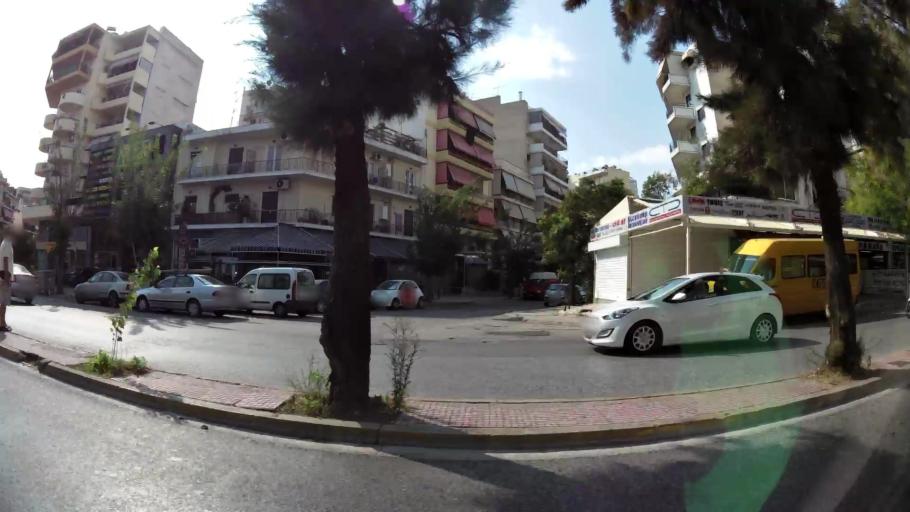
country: GR
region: Attica
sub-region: Nomarchia Athinas
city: Kipseli
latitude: 38.0066
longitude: 23.7166
